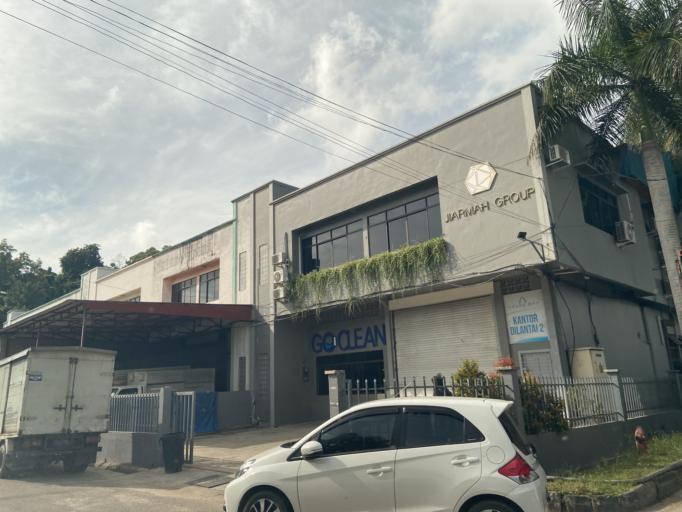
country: SG
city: Singapore
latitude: 1.1475
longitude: 104.0203
